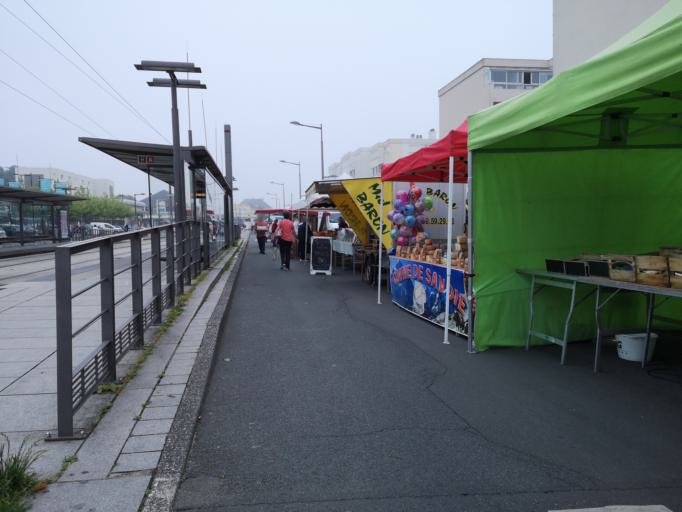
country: FR
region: Centre
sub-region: Departement du Loiret
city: Fleury-les-Aubrais
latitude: 47.9282
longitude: 1.9197
